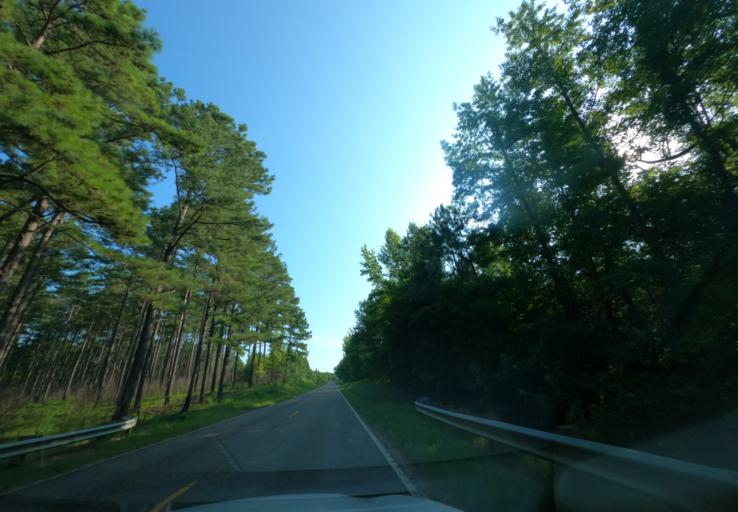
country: US
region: South Carolina
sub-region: Edgefield County
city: Edgefield
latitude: 33.7514
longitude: -81.9577
